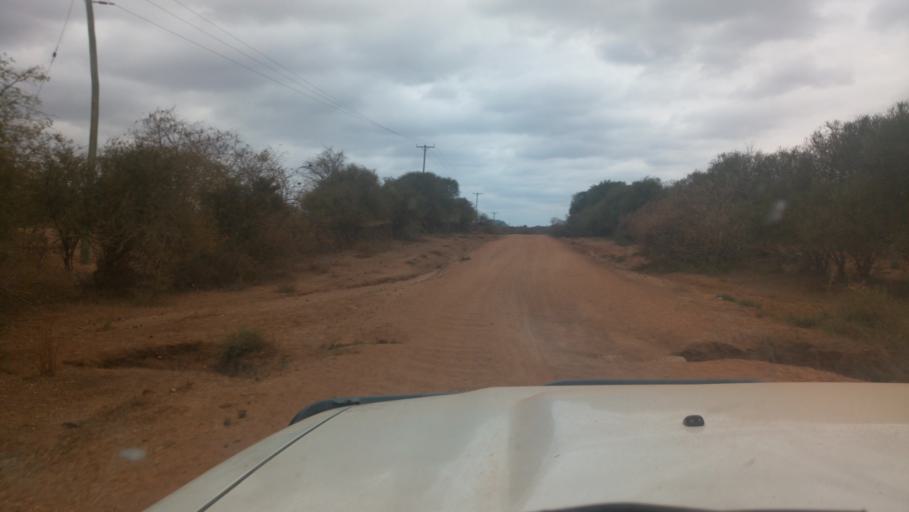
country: KE
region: Makueni
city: Wote
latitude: -1.9132
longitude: 38.0225
